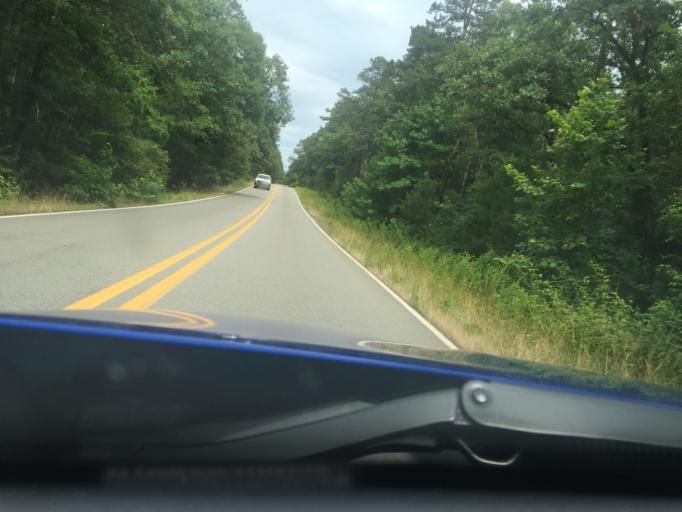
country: US
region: Arkansas
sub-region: Pulaski County
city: Maumelle
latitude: 34.8353
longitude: -92.4658
